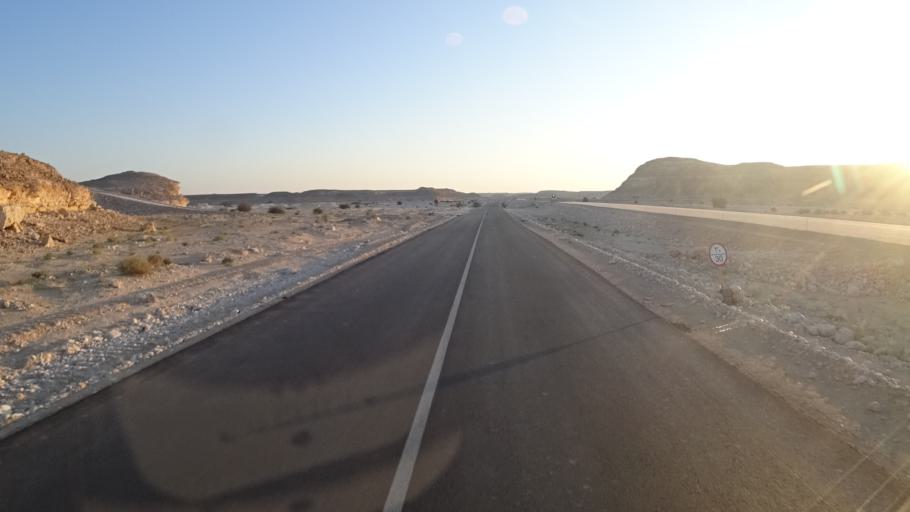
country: OM
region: Zufar
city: Salalah
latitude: 17.5224
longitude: 53.3777
